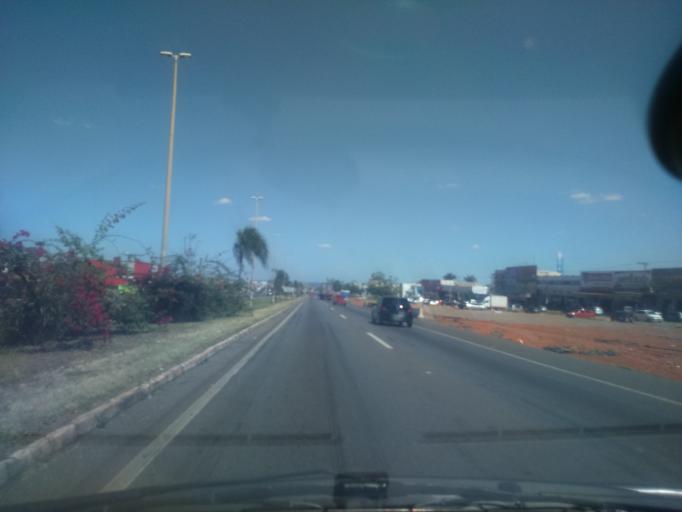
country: BR
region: Goias
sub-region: Luziania
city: Luziania
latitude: -16.0571
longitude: -47.9827
